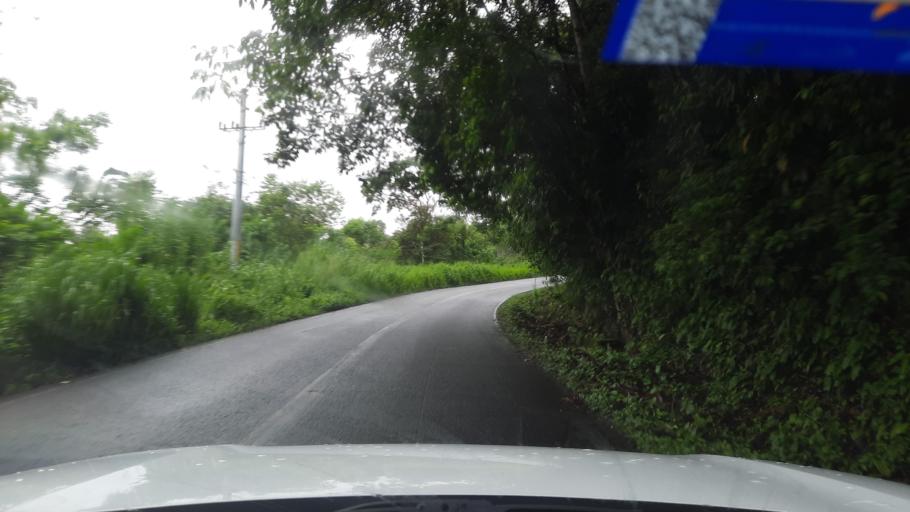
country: CR
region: Alajuela
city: Bijagua
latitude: 10.7790
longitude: -85.0278
